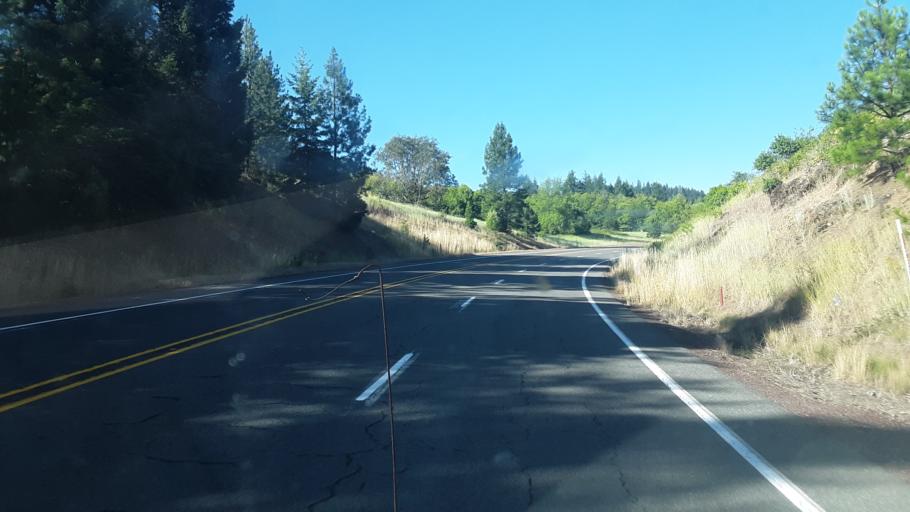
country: US
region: Oregon
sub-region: Jackson County
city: Shady Cove
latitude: 42.6903
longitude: -122.6008
